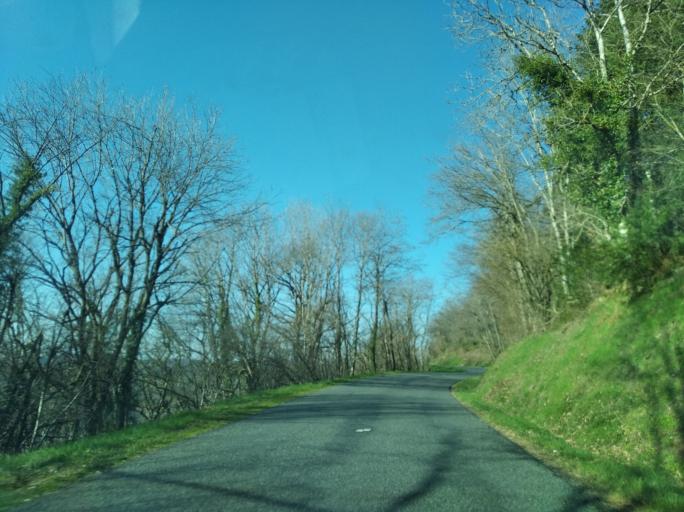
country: FR
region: Auvergne
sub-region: Departement de l'Allier
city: Le Mayet-de-Montagne
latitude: 46.1054
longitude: 3.6802
